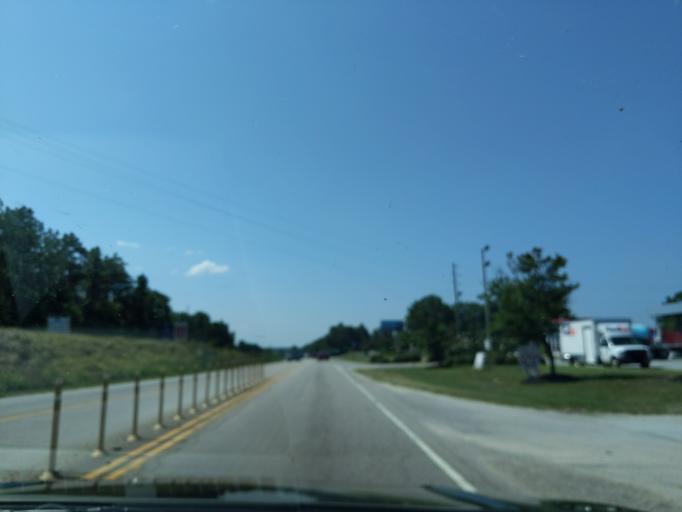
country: US
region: South Carolina
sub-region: Lexington County
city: Red Bank
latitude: 33.9318
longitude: -81.2907
